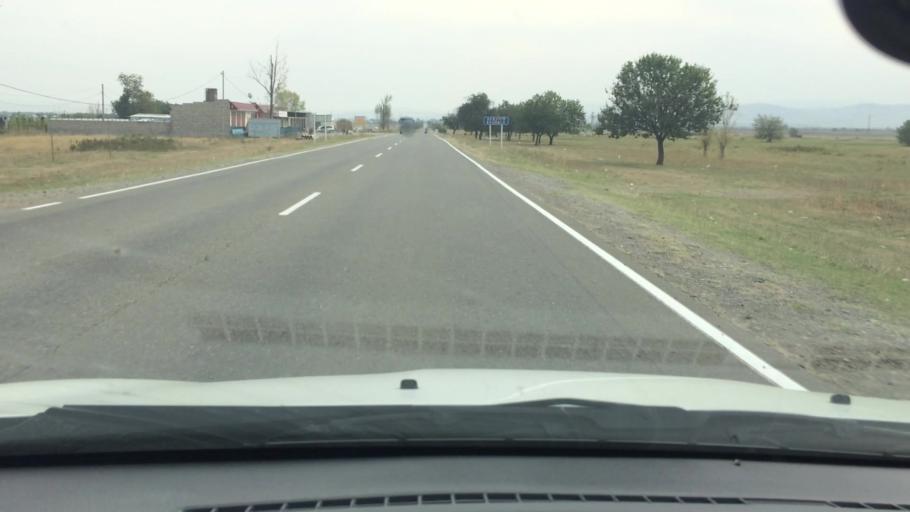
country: GE
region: Kvemo Kartli
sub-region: Gardabani
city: Gardabani
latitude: 41.4432
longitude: 44.9990
